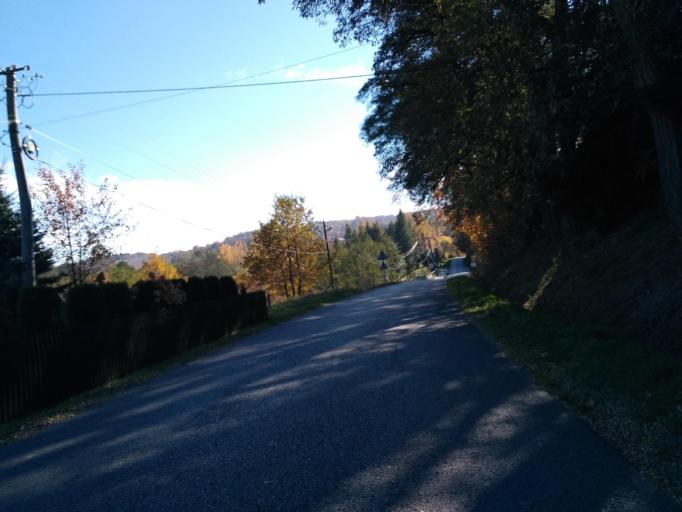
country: PL
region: Subcarpathian Voivodeship
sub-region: Powiat ropczycko-sedziszowski
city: Iwierzyce
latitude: 49.9840
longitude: 21.7259
